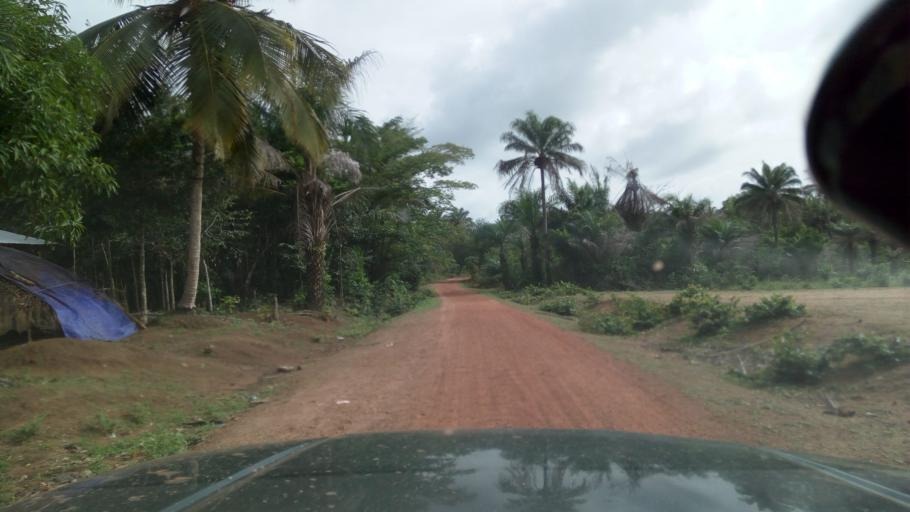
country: SL
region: Northern Province
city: Port Loko
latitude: 8.7880
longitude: -12.9252
